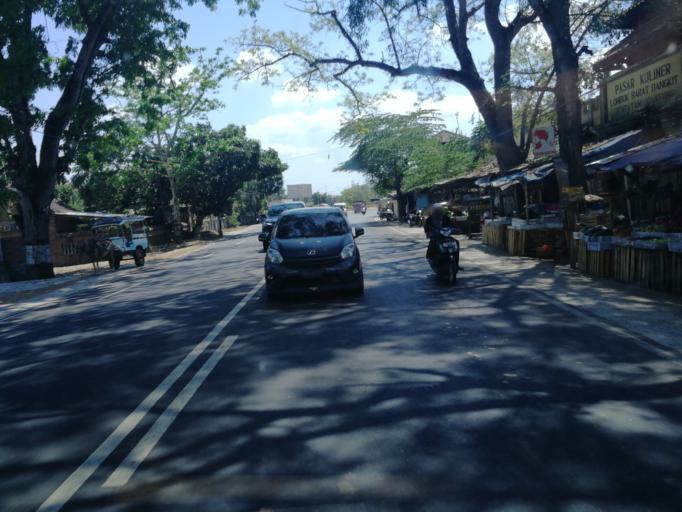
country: ID
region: West Nusa Tenggara
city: Jelateng Timur
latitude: -8.6925
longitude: 116.1102
